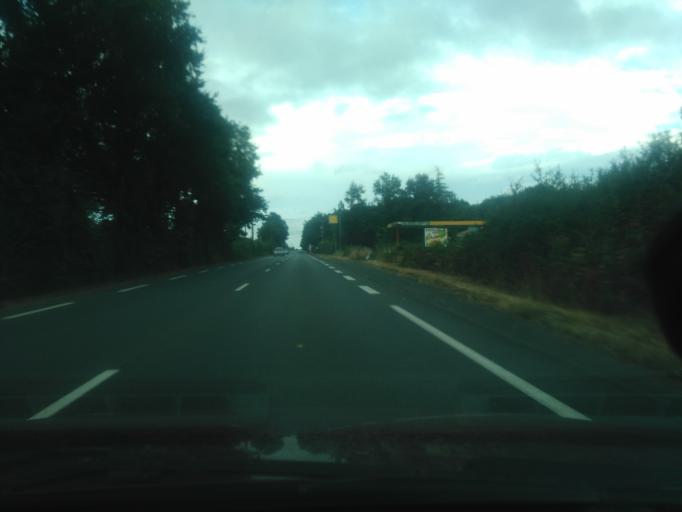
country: FR
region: Pays de la Loire
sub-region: Departement de la Vendee
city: La Ferriere
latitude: 46.6972
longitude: -1.3541
